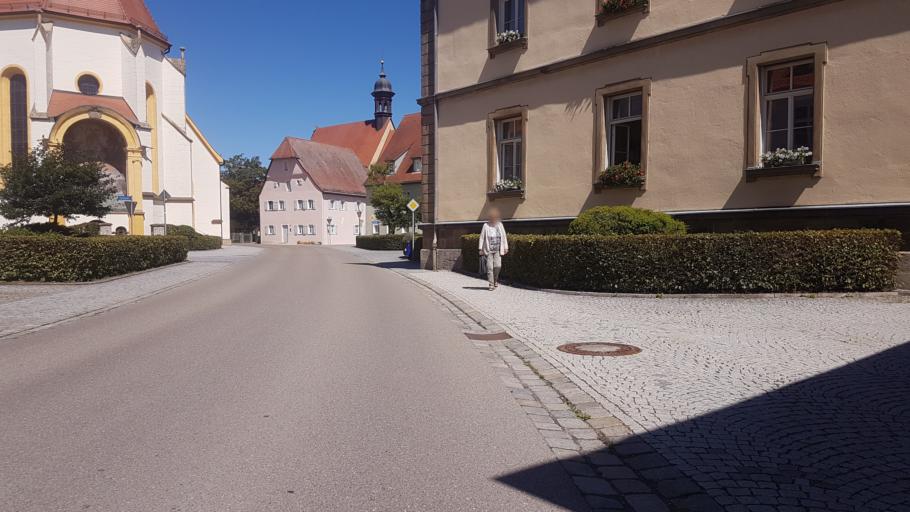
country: DE
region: Bavaria
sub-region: Regierungsbezirk Mittelfranken
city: Herrieden
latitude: 49.2320
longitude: 10.4995
